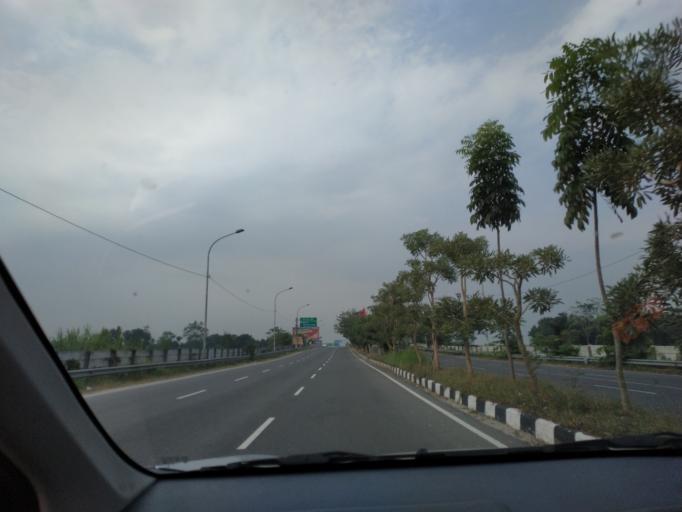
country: ID
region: North Sumatra
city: Percut
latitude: 3.6036
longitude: 98.8475
